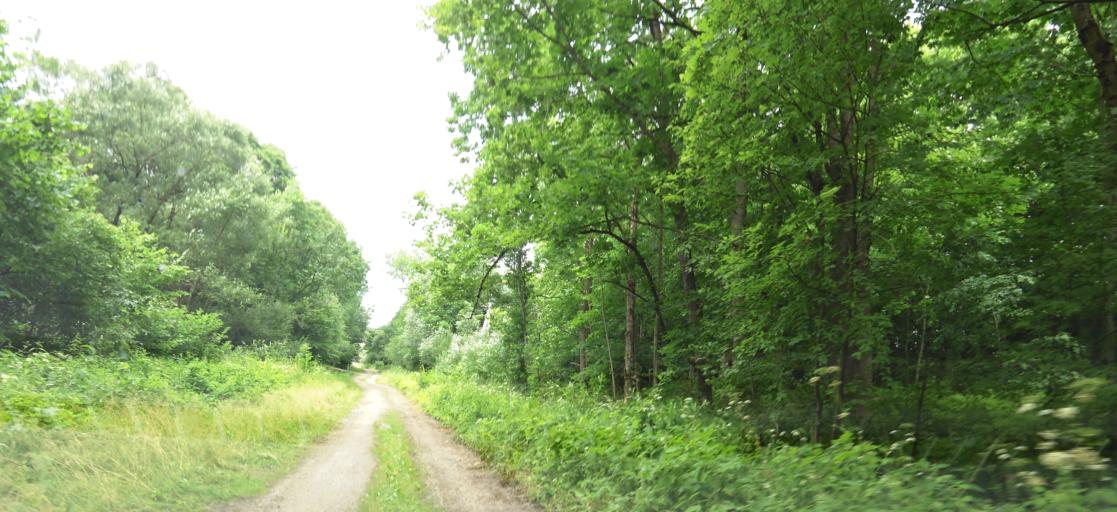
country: LT
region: Vilnius County
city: Ukmerge
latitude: 55.2094
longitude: 24.7944
